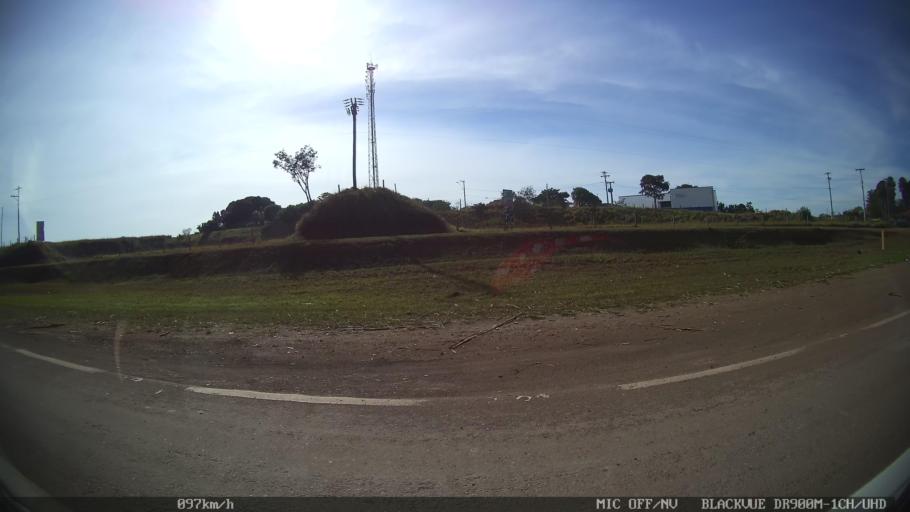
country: BR
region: Sao Paulo
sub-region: Rio Das Pedras
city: Rio das Pedras
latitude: -22.7863
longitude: -47.5850
